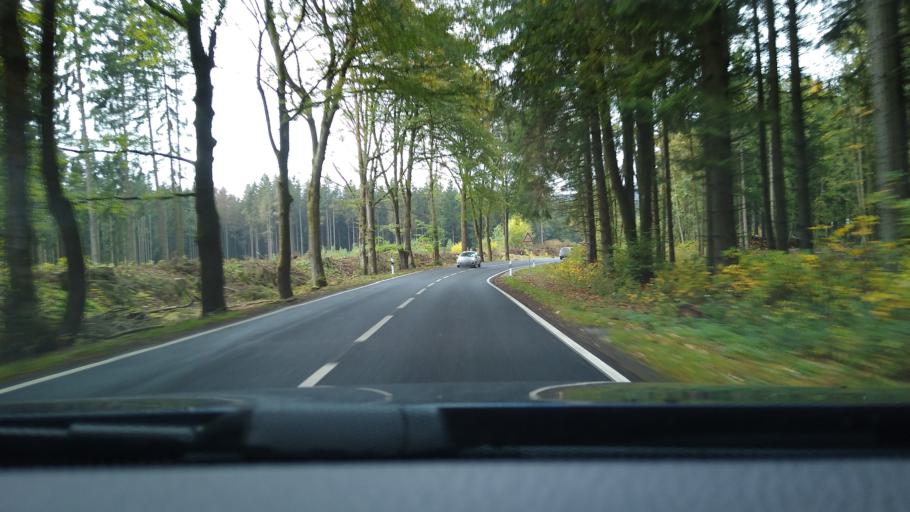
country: DE
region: Saxony-Anhalt
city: Elbingerode
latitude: 51.7705
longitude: 10.7353
